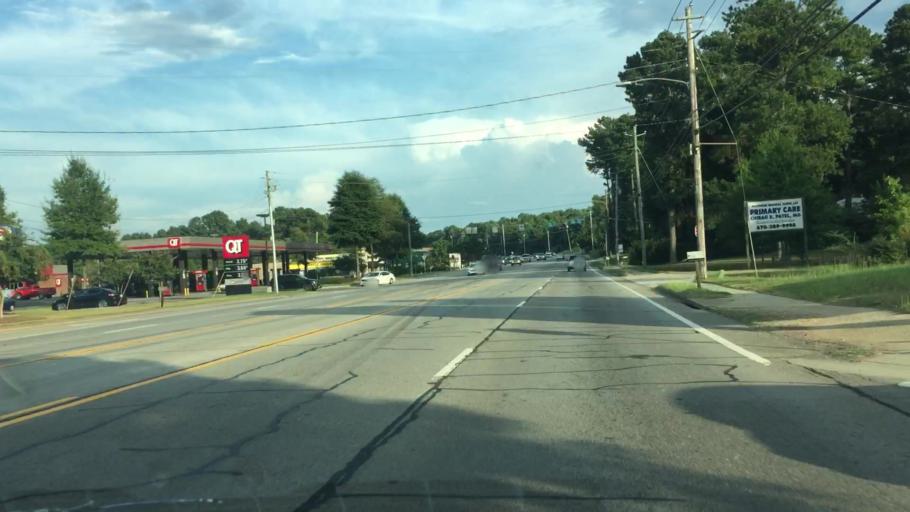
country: US
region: Georgia
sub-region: Henry County
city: Stockbridge
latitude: 33.5483
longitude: -84.2526
